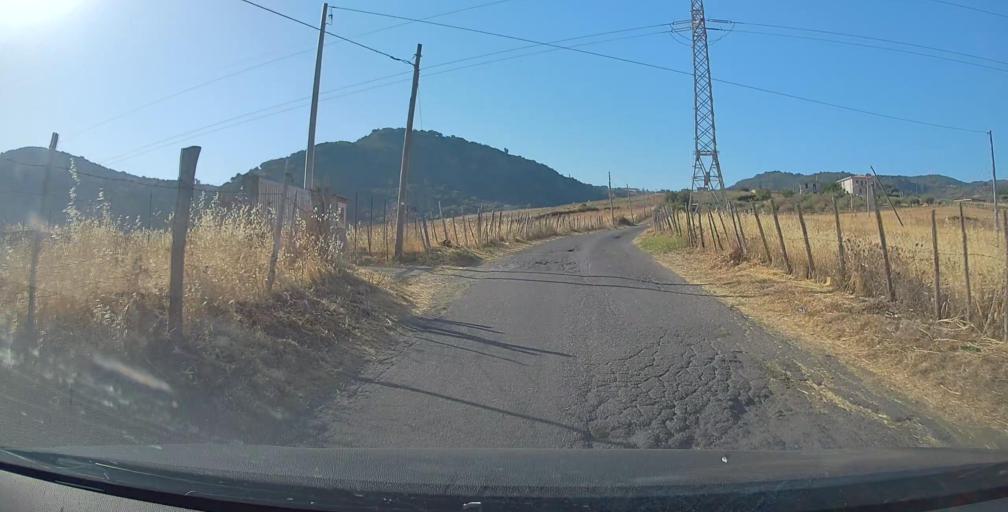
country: IT
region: Sicily
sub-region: Messina
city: San Piero Patti
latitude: 38.0716
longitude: 14.9855
